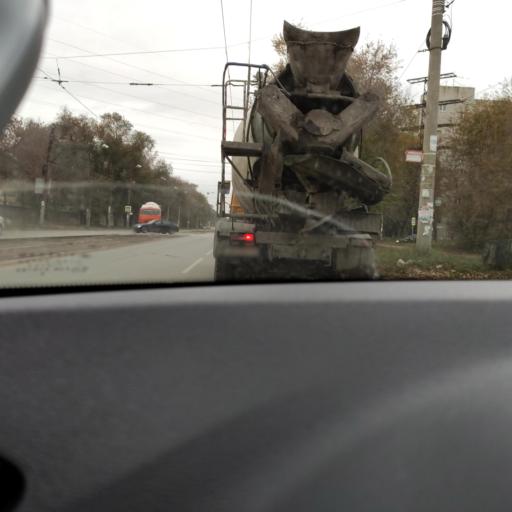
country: RU
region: Samara
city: Smyshlyayevka
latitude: 53.1989
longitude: 50.2869
